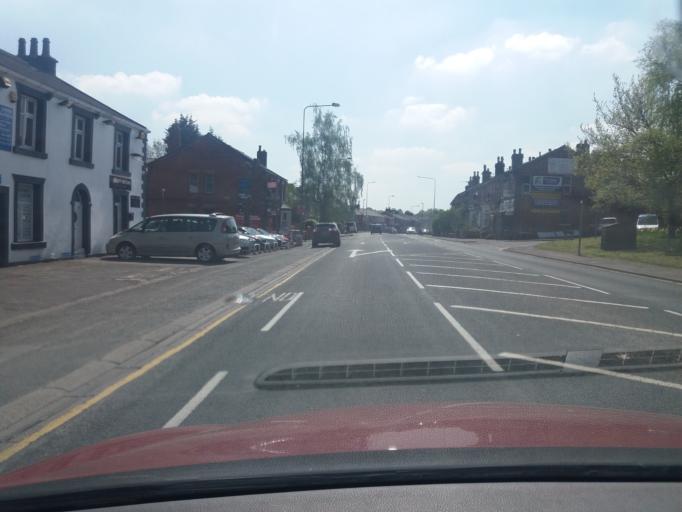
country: GB
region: England
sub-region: Lancashire
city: Clayton-le-Woods
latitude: 53.6956
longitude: -2.6385
